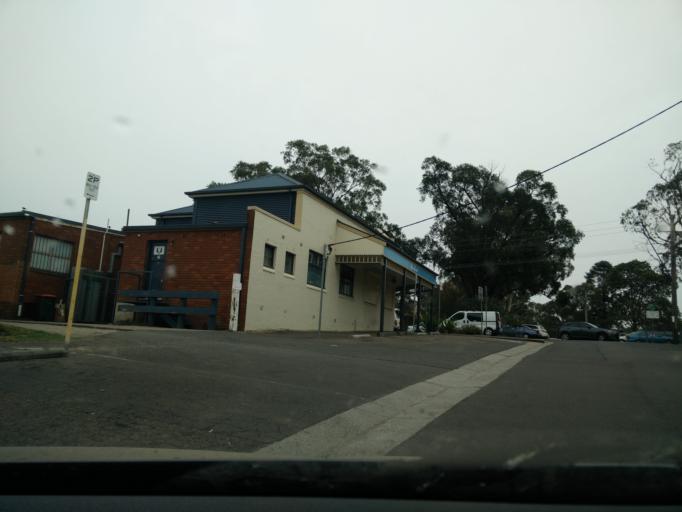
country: AU
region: New South Wales
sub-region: Blue Mountains Municipality
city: Glenbrook
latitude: -33.7672
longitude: 150.6230
